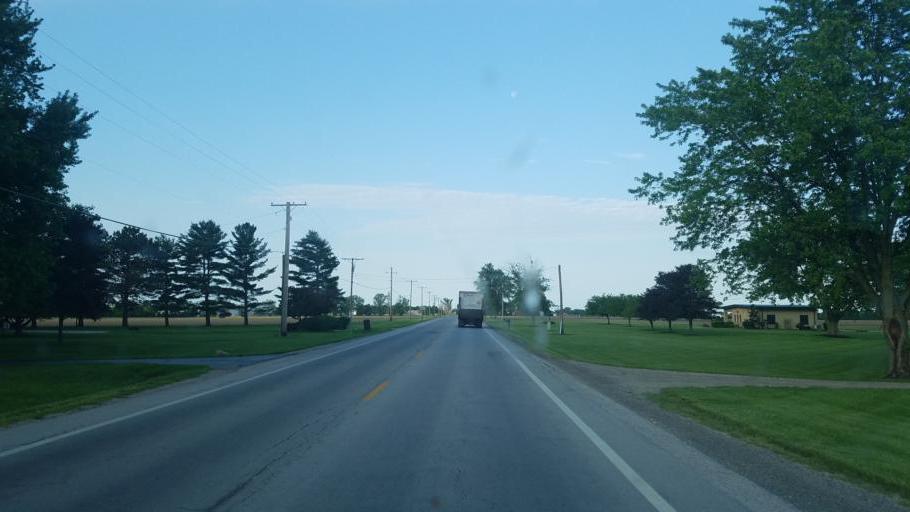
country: US
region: Ohio
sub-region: Fayette County
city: Washington Court House
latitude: 39.5592
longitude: -83.4139
